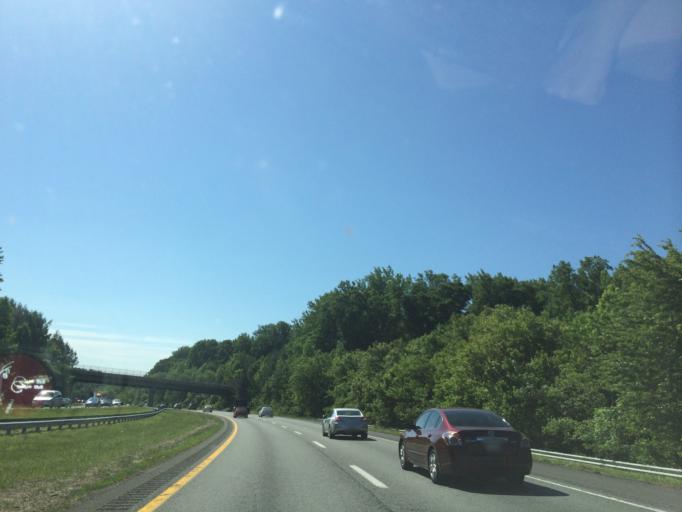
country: US
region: Maryland
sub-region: Anne Arundel County
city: Crownsville
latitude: 39.0087
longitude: -76.6104
